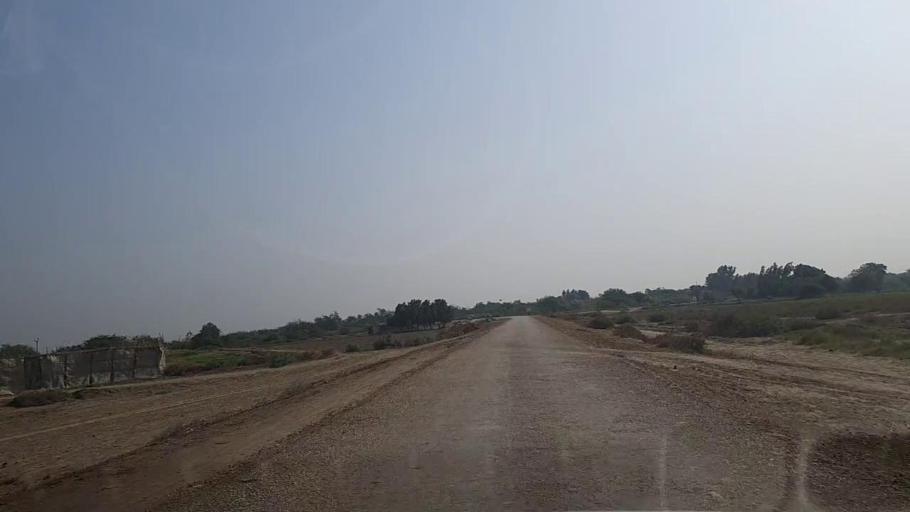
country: PK
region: Sindh
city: Keti Bandar
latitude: 24.2453
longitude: 67.6998
